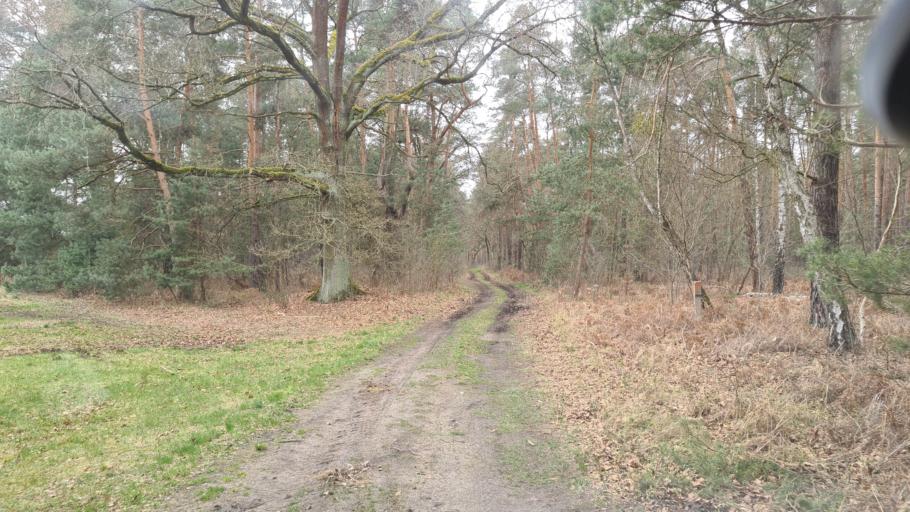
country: DE
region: Brandenburg
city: Finsterwalde
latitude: 51.5656
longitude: 13.6890
